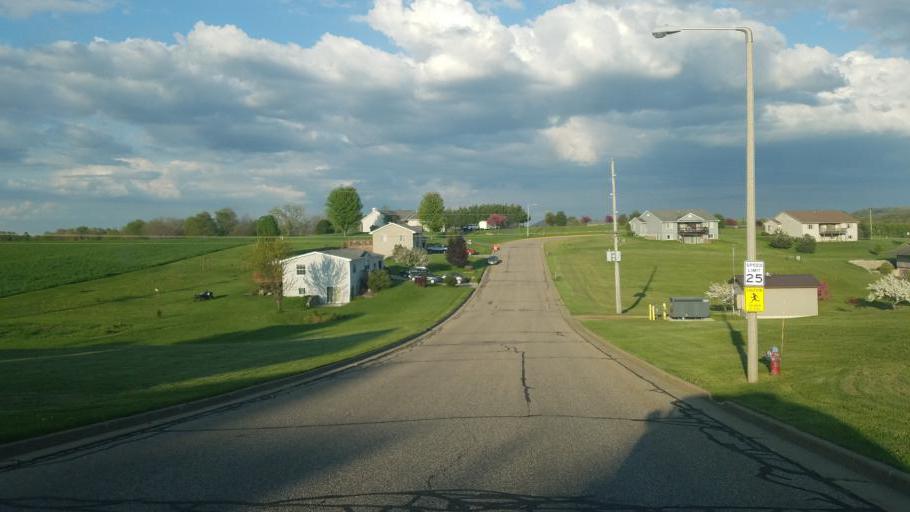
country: US
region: Wisconsin
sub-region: Vernon County
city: Hillsboro
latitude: 43.6617
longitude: -90.3402
